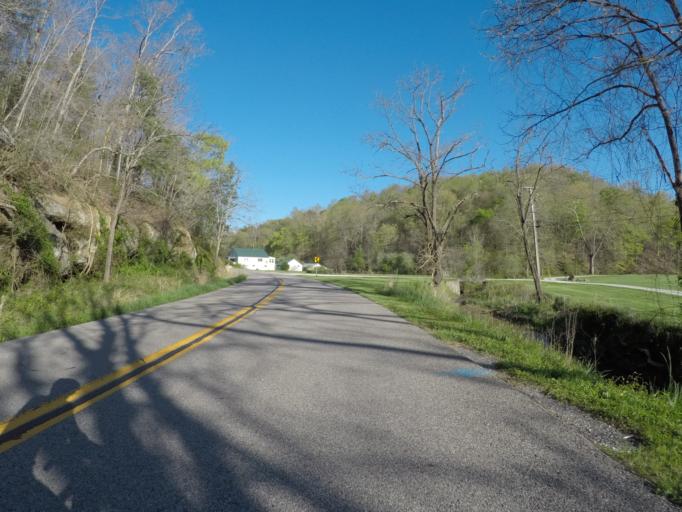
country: US
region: Kentucky
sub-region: Boyd County
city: Meads
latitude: 38.3636
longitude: -82.6773
